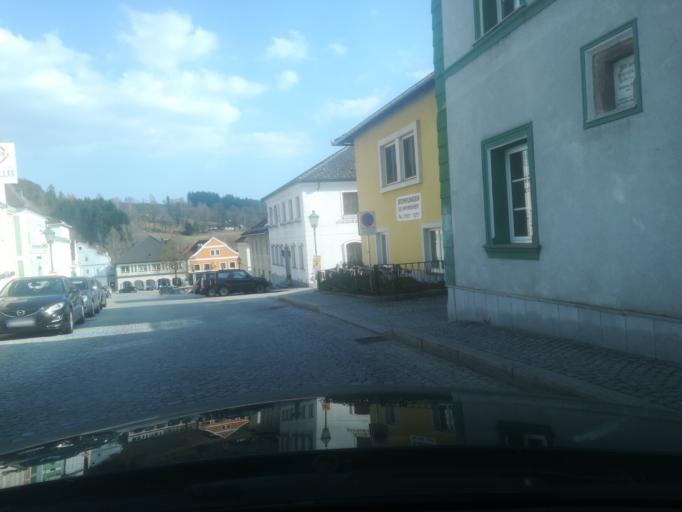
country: AT
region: Upper Austria
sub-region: Politischer Bezirk Perg
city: Perg
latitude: 48.3504
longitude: 14.6685
